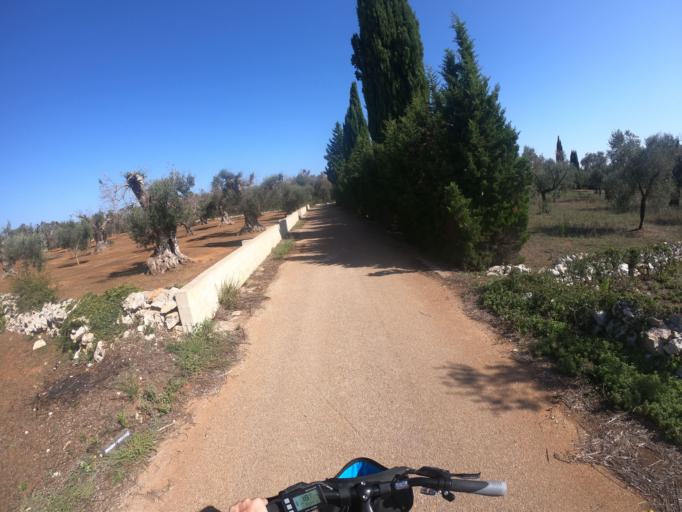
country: IT
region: Apulia
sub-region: Provincia di Lecce
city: Specchia
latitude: 39.9193
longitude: 18.2856
